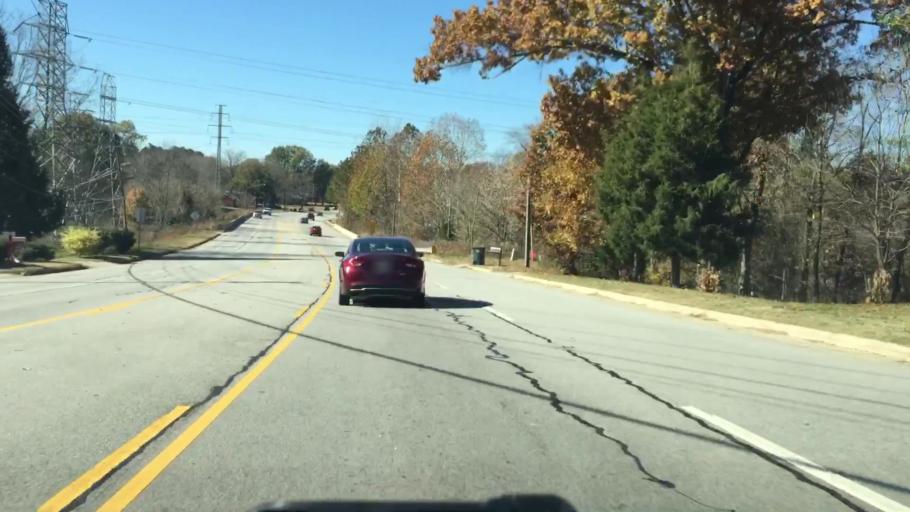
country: US
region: North Carolina
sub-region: Rowan County
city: Salisbury
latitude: 35.6640
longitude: -80.5077
